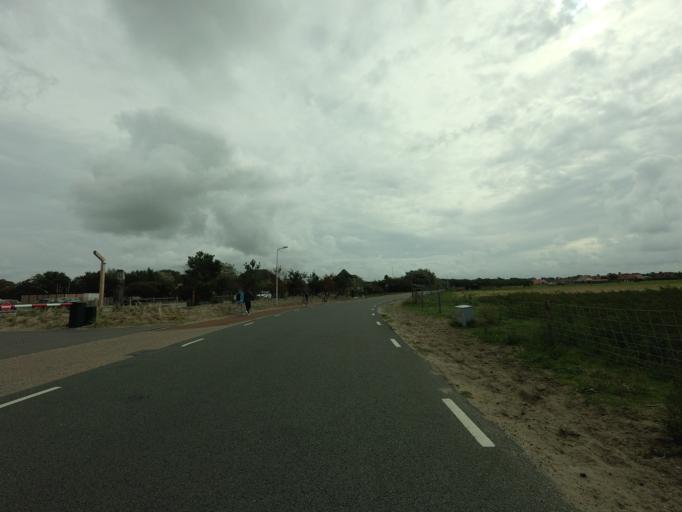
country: NL
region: Friesland
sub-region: Gemeente Ameland
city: Hollum
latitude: 53.4479
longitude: 5.6313
